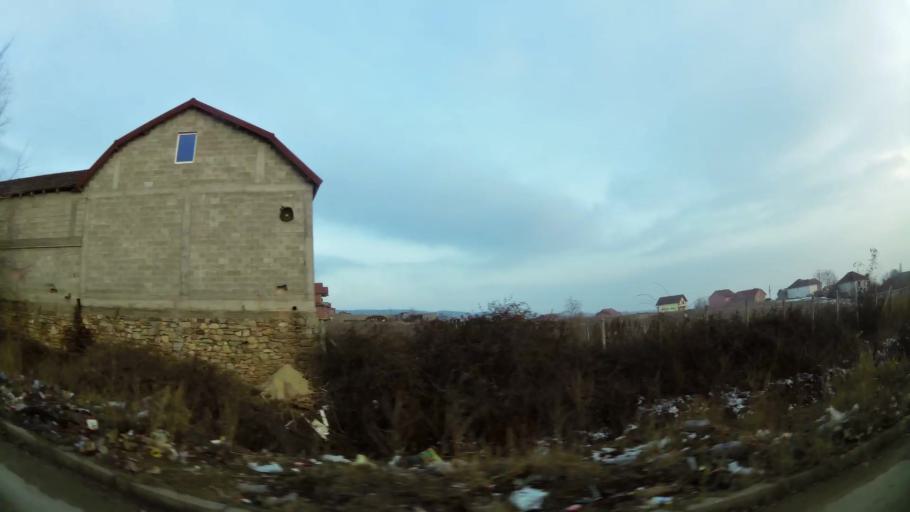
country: MK
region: Aracinovo
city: Arachinovo
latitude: 42.0273
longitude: 21.5739
